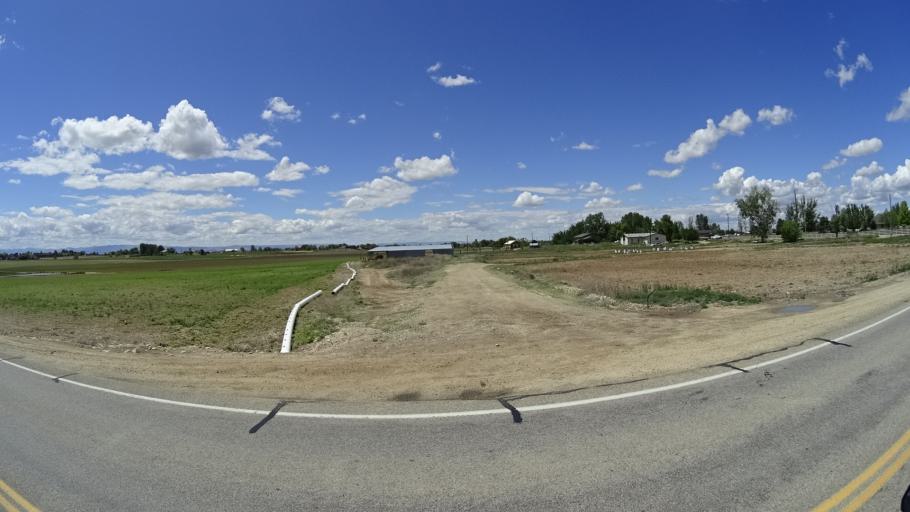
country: US
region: Idaho
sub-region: Ada County
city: Meridian
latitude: 43.5745
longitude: -116.4335
